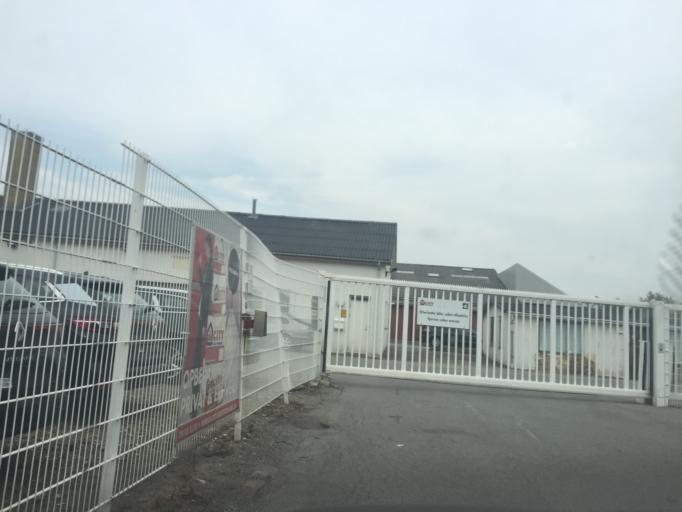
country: DK
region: Capital Region
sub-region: Albertslund Kommune
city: Albertslund
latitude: 55.6627
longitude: 12.3699
